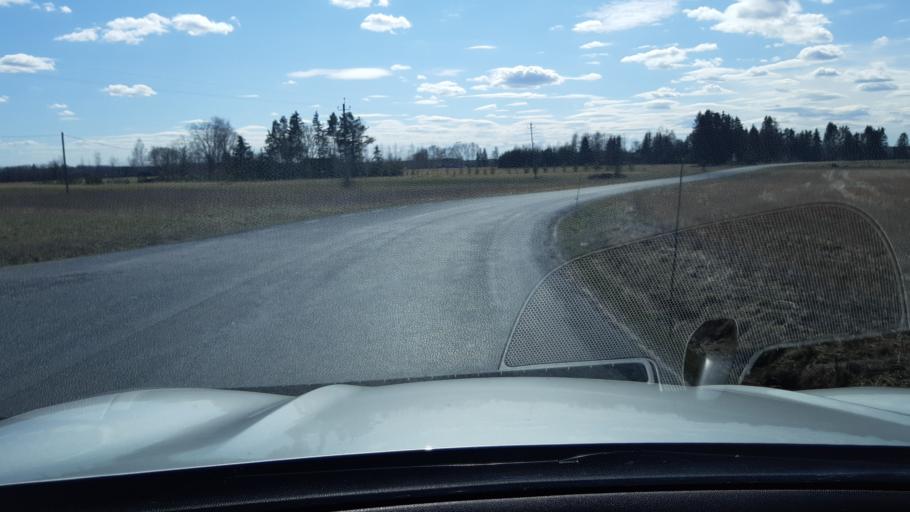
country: EE
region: Raplamaa
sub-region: Kohila vald
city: Kohila
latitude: 59.1865
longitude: 24.8731
